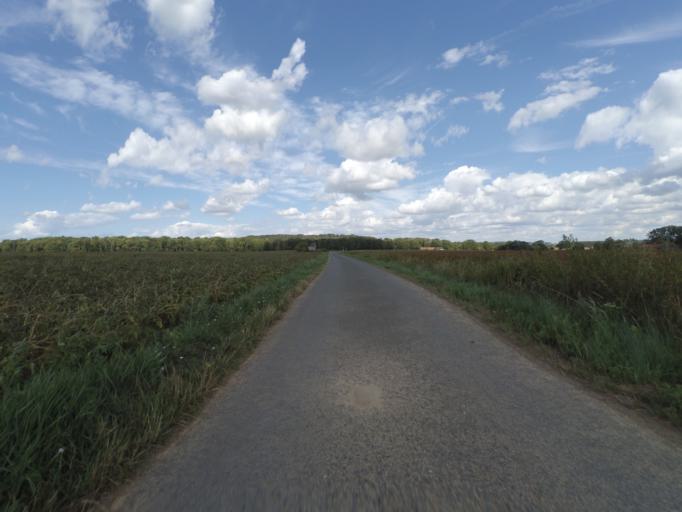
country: BE
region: Wallonia
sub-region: Province du Hainaut
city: Frasnes-lez-Buissenal
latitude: 50.6689
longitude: 3.5796
